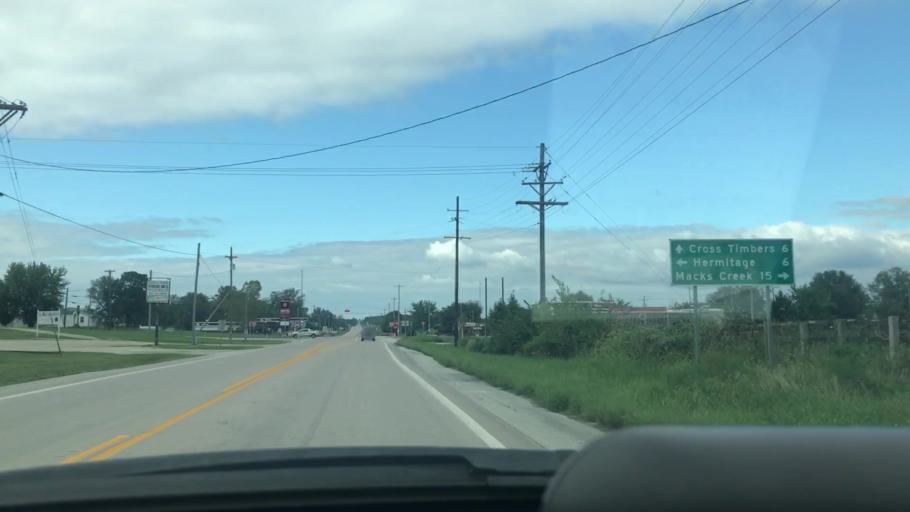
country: US
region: Missouri
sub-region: Hickory County
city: Hermitage
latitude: 37.9393
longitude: -93.2081
